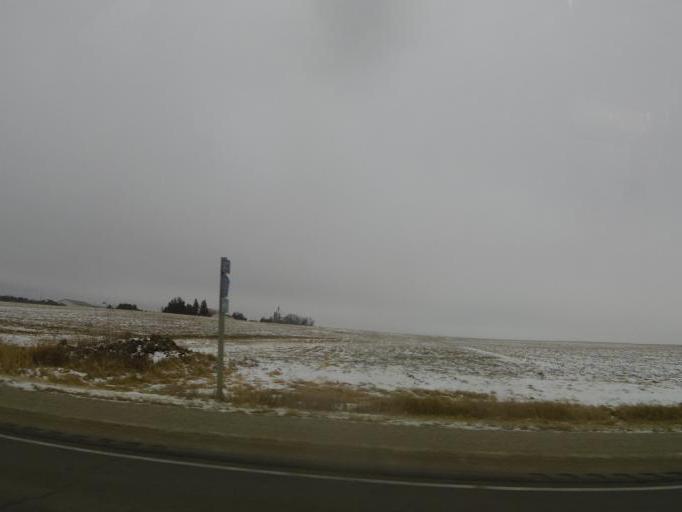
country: US
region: Iowa
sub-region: Howard County
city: Cresco
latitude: 43.4415
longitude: -92.2989
